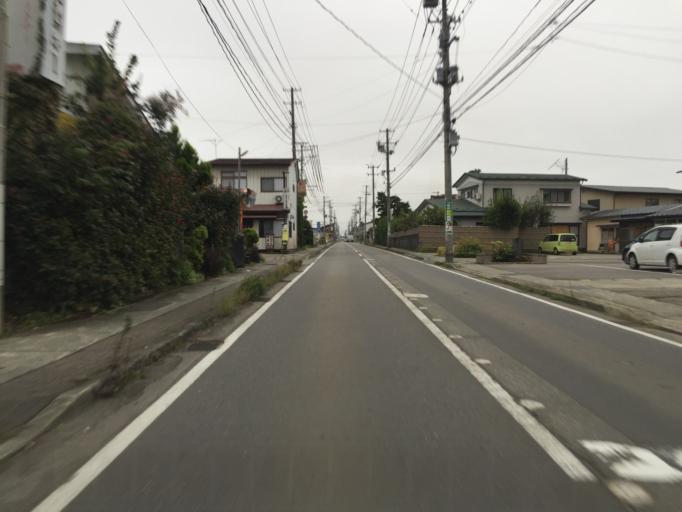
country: JP
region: Fukushima
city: Kitakata
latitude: 37.4742
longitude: 139.9243
